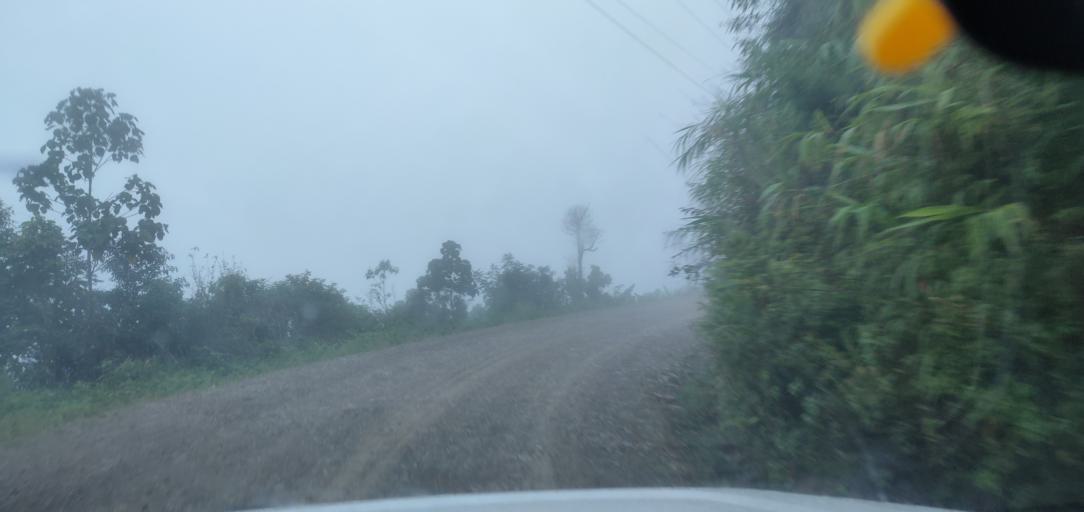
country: LA
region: Phongsali
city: Phongsali
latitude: 21.3933
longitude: 102.1923
